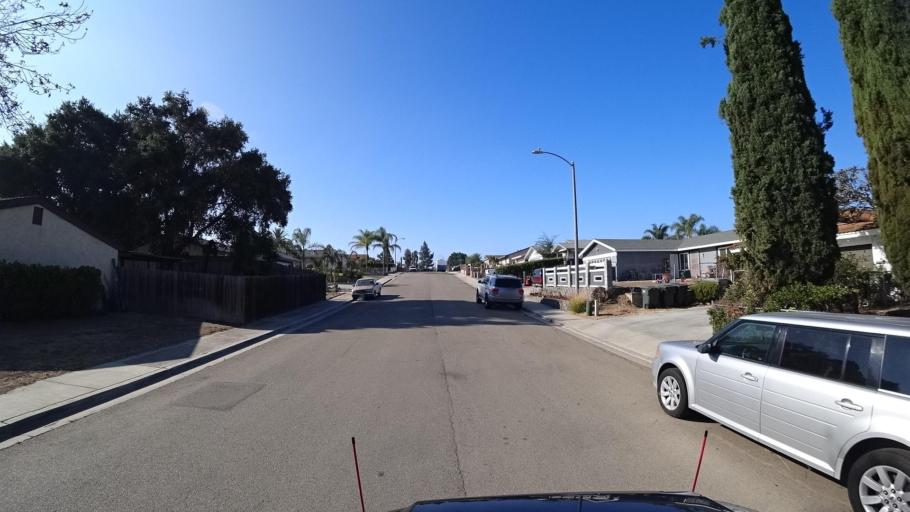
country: US
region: California
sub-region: San Diego County
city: Fallbrook
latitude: 33.3755
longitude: -117.2333
